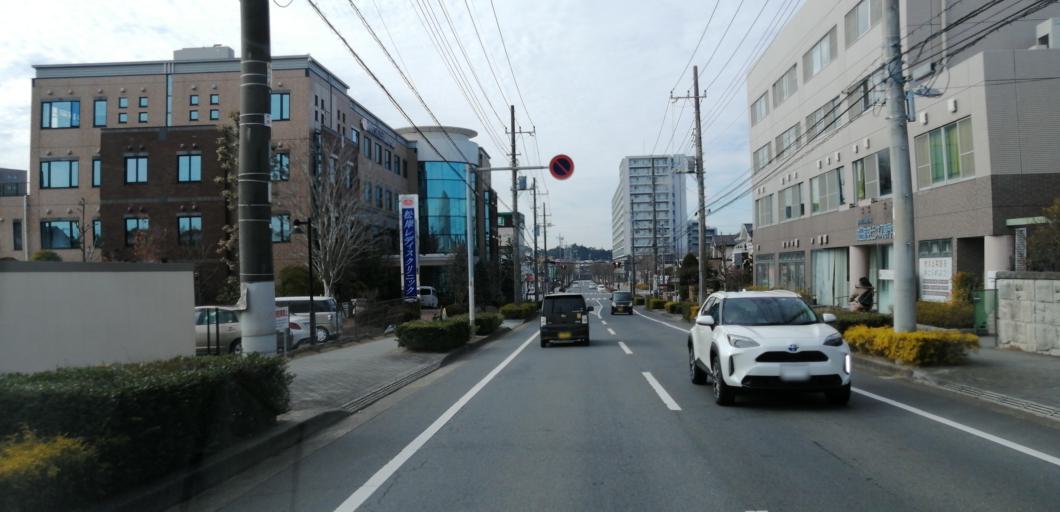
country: JP
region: Chiba
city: Narita
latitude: 35.7590
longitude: 140.2994
